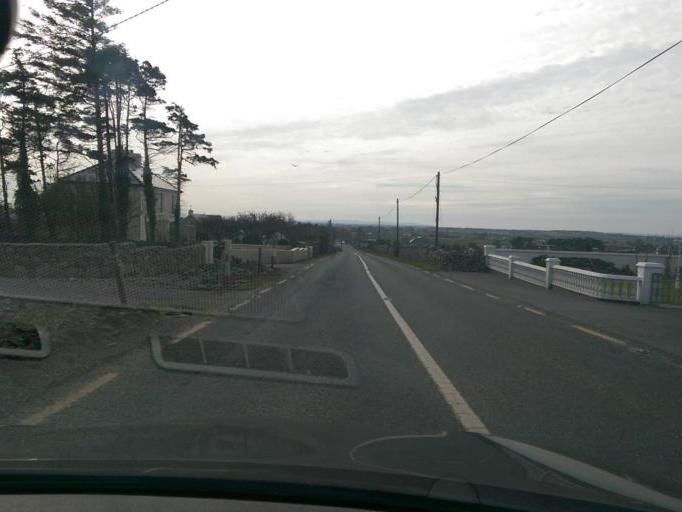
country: IE
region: Connaught
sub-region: County Galway
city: Tuam
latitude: 53.4041
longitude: -8.8265
